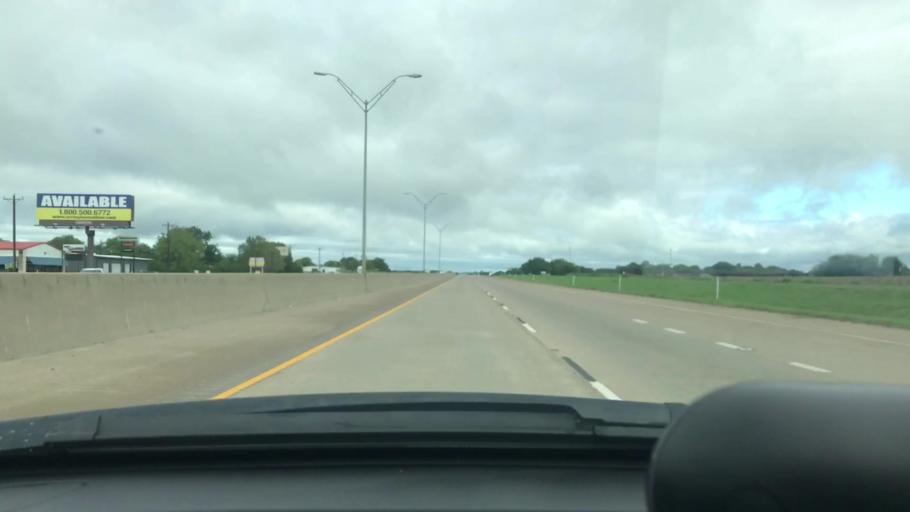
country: US
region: Texas
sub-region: Grayson County
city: Van Alstyne
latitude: 33.4342
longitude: -96.5953
